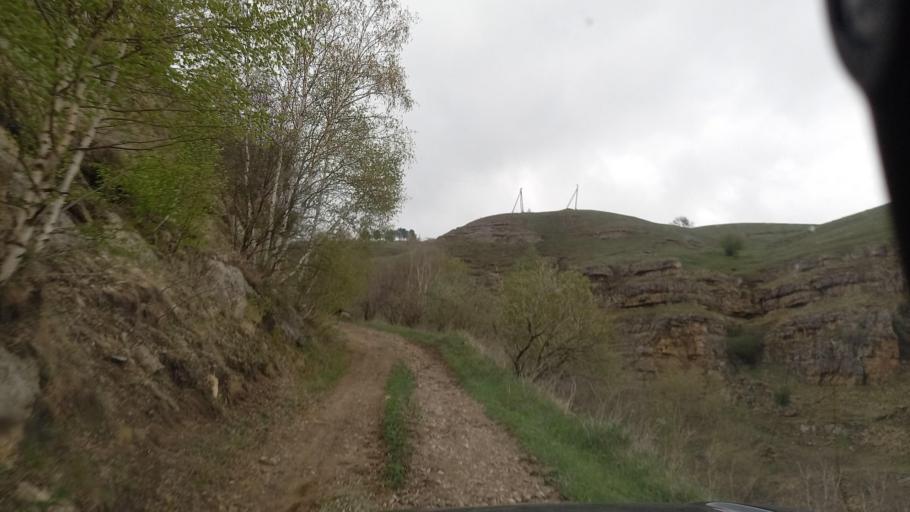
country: RU
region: Stavropol'skiy
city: Nezhinskiy
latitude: 43.8537
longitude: 42.6384
